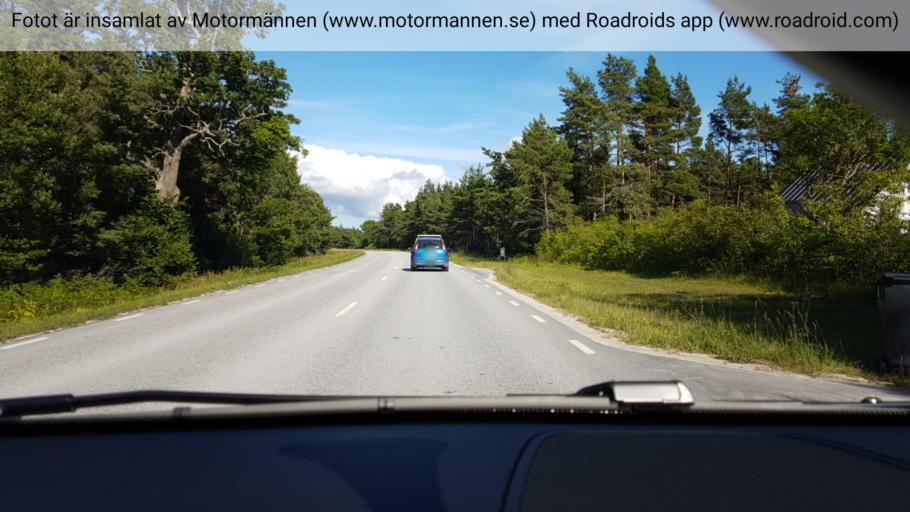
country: SE
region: Gotland
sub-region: Gotland
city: Slite
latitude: 57.7451
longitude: 18.6837
